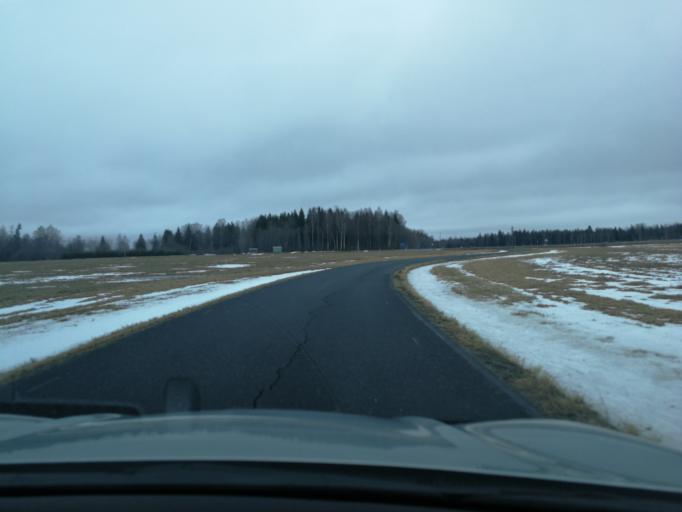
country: EE
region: Harju
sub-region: Rae vald
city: Vaida
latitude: 59.2340
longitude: 25.0203
